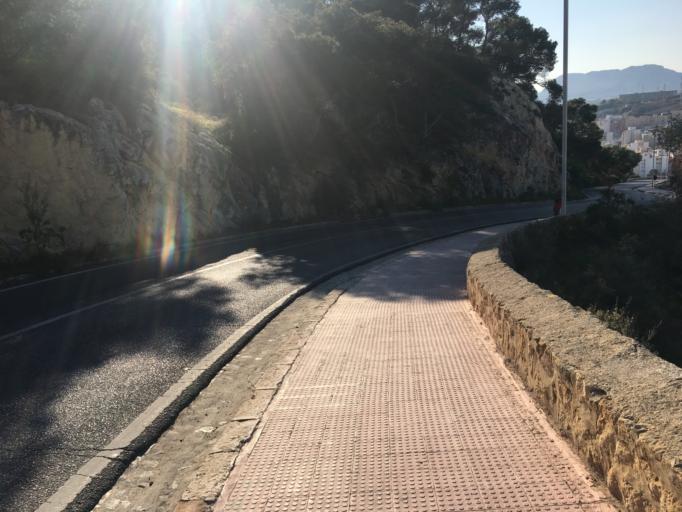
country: ES
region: Valencia
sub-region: Provincia de Alicante
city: Alicante
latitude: 38.3497
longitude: -0.4784
